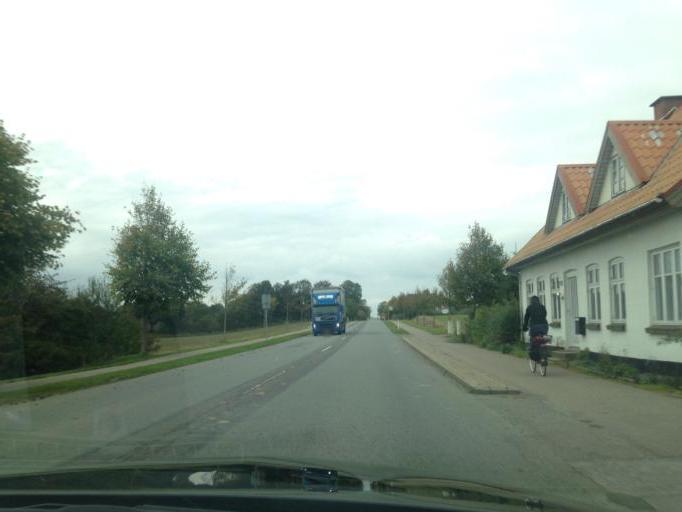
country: DK
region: South Denmark
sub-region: Kolding Kommune
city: Christiansfeld
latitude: 55.3805
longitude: 9.4808
